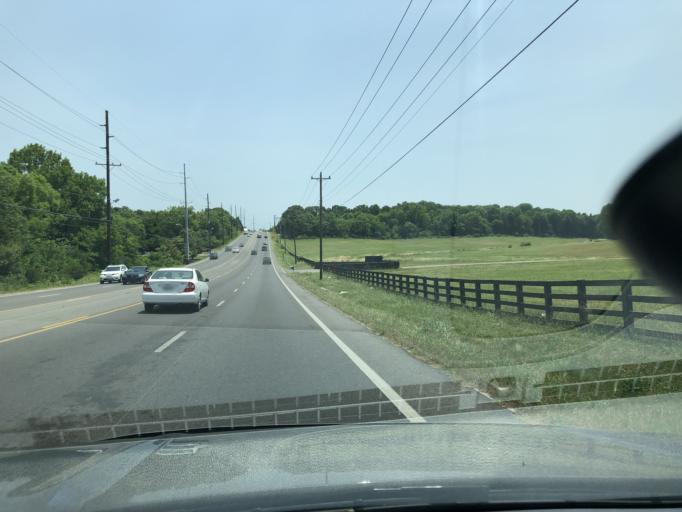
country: US
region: Tennessee
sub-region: Rutherford County
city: La Vergne
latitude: 36.0622
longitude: -86.6257
